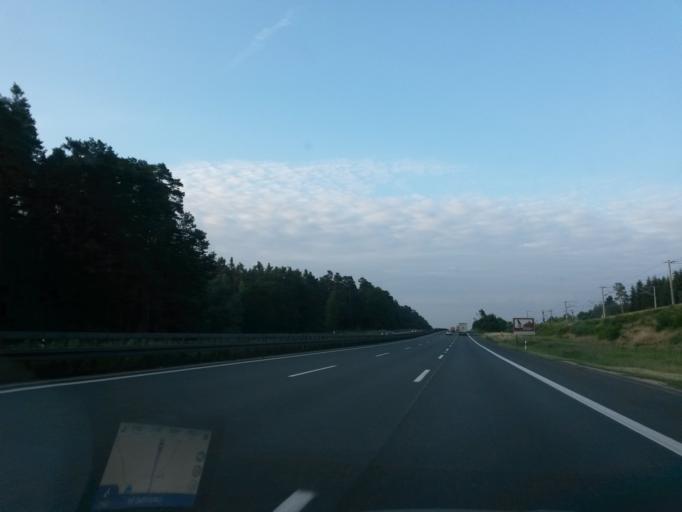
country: DE
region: Bavaria
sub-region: Regierungsbezirk Mittelfranken
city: Allersberg
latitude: 49.2731
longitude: 11.2106
